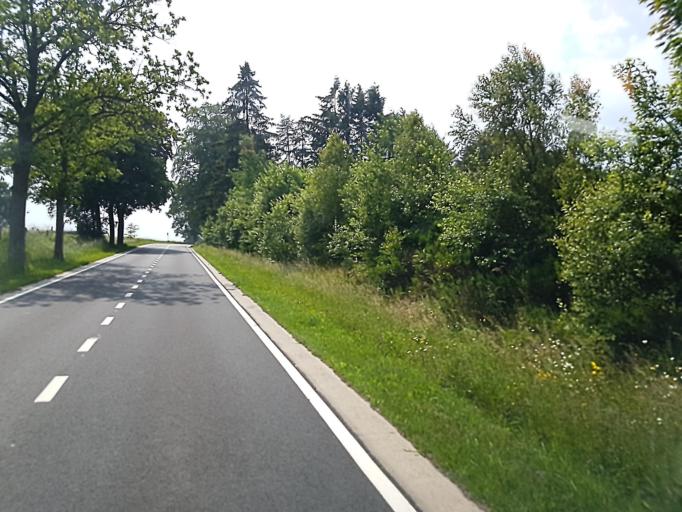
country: BE
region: Wallonia
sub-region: Province de Liege
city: Lierneux
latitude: 50.3346
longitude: 5.7845
